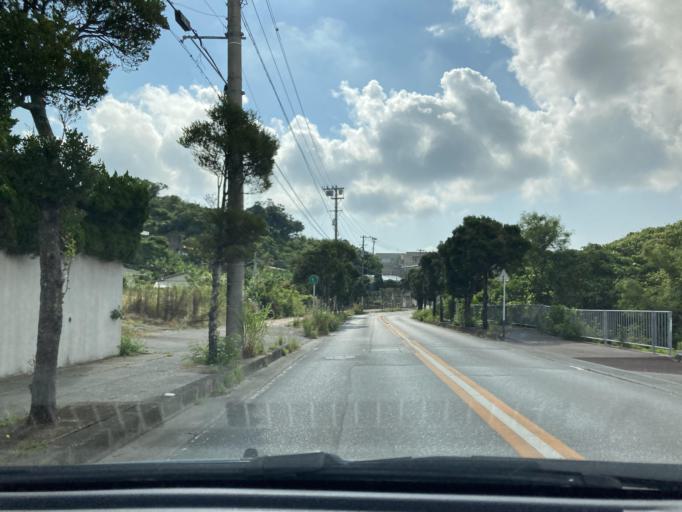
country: JP
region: Okinawa
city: Tomigusuku
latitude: 26.1471
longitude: 127.7627
